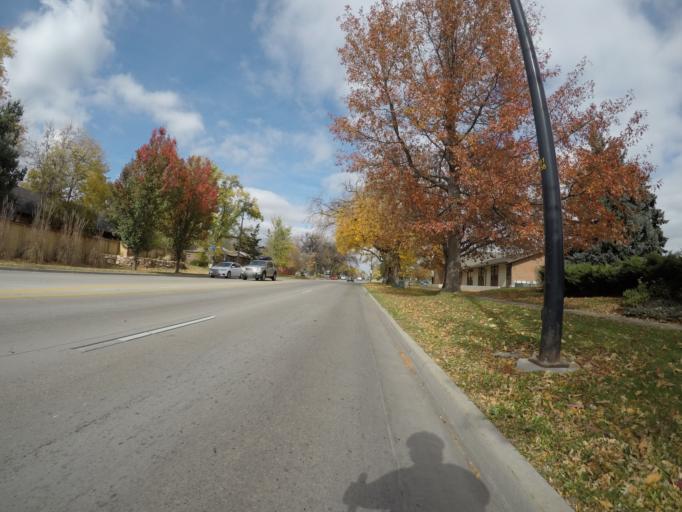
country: US
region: Colorado
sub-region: Boulder County
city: Boulder
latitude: 40.0325
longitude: -105.2820
